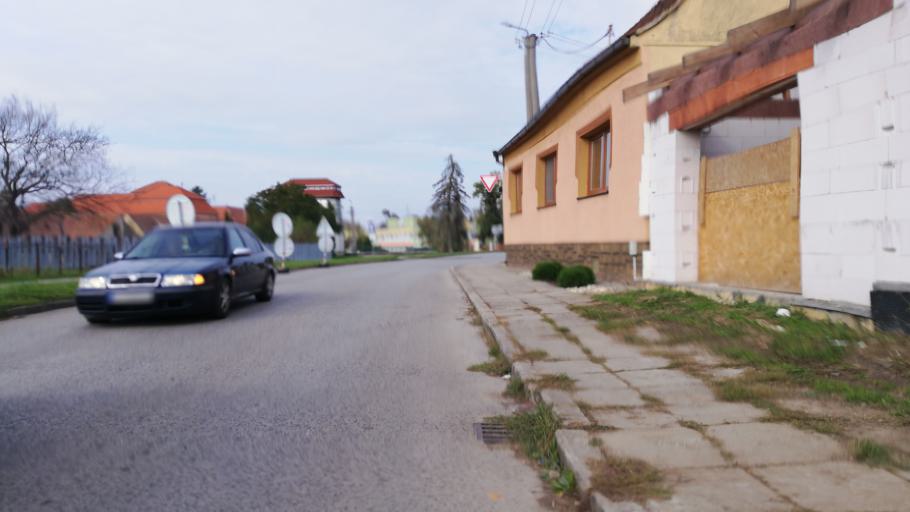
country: SK
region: Trnavsky
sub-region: Okres Skalica
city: Skalica
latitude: 48.8462
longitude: 17.2343
